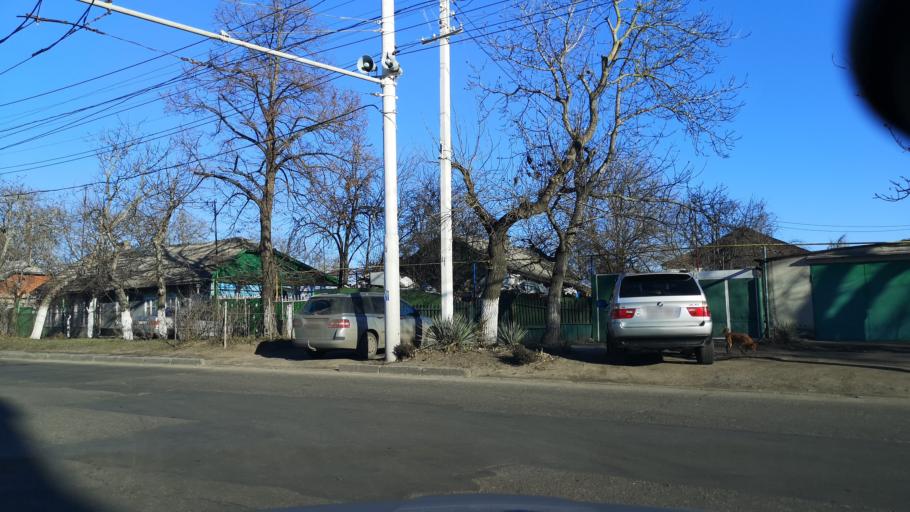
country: MD
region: Bender
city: Bender
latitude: 46.8292
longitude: 29.4877
